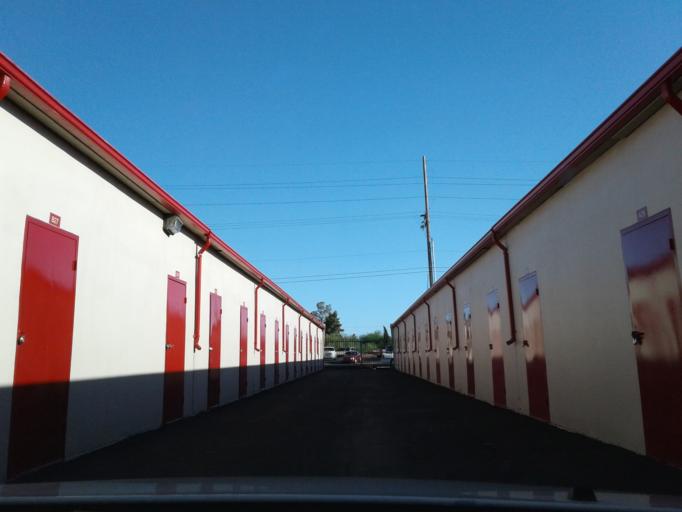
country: US
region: Arizona
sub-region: Pima County
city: Tucson
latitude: 32.2004
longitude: -110.9074
